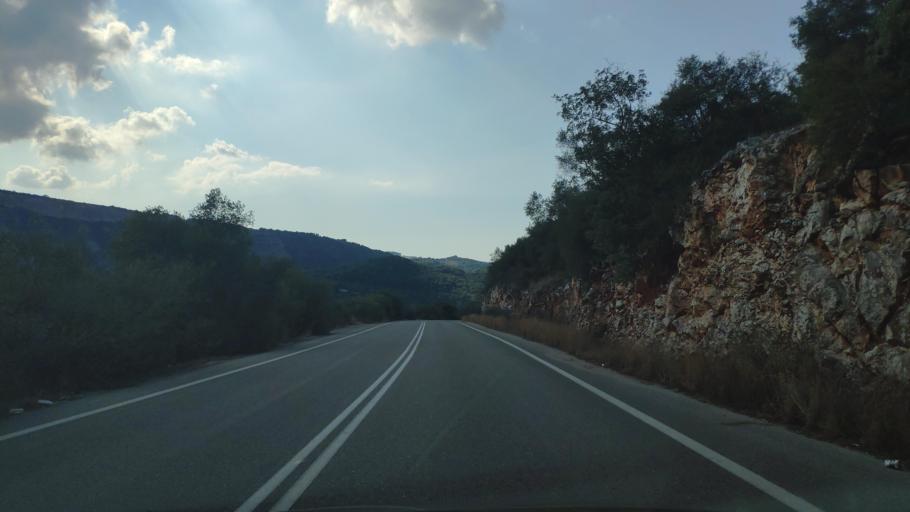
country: GR
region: West Greece
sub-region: Nomos Aitolias kai Akarnanias
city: Stanos
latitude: 38.7695
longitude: 21.1605
